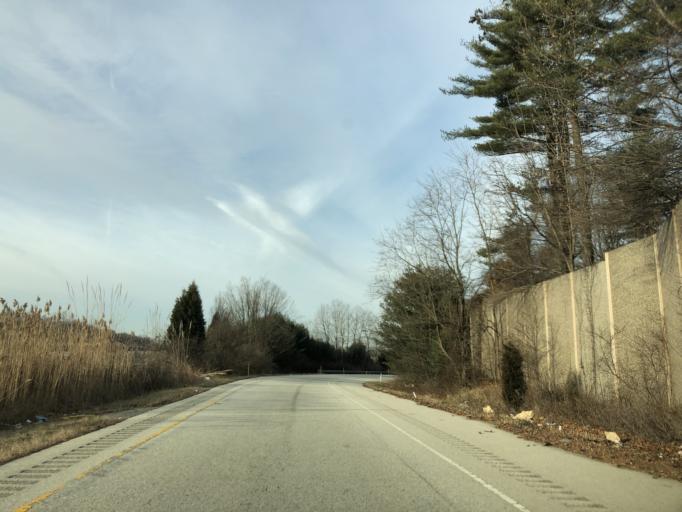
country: US
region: Pennsylvania
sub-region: Chester County
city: Exton
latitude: 40.0219
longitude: -75.6199
